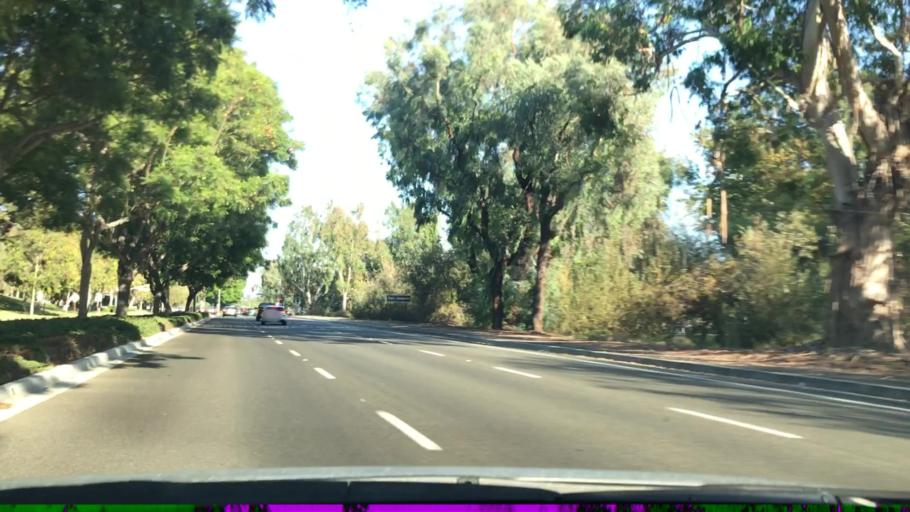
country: US
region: California
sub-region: Orange County
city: Irvine
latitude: 33.6575
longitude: -117.8338
